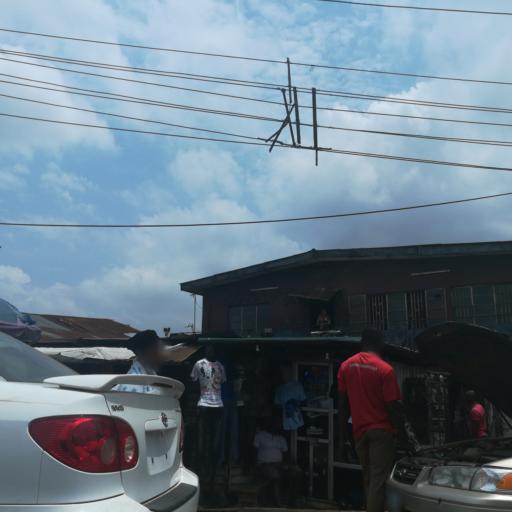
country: NG
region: Lagos
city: Ojota
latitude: 6.5877
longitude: 3.3814
